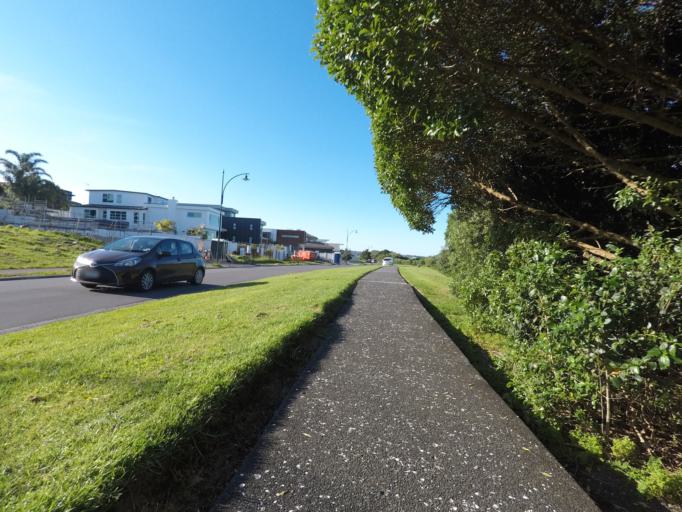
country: NZ
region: Auckland
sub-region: Auckland
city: Rosebank
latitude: -36.8357
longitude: 174.6618
